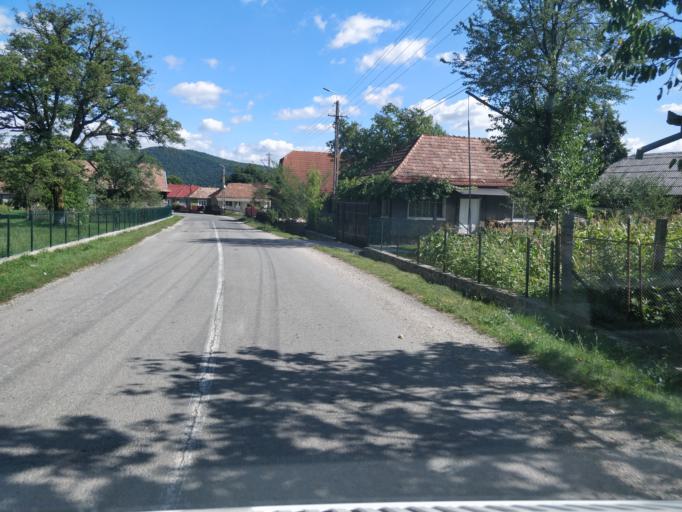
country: RO
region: Cluj
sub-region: Comuna Poeni
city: Poeni
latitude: 46.8736
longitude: 22.8788
